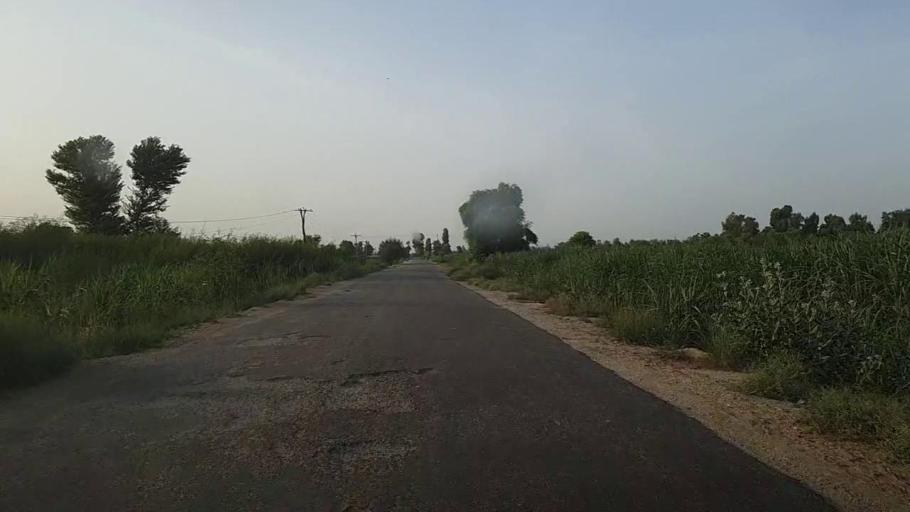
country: PK
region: Sindh
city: Ubauro
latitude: 28.1844
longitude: 69.8281
